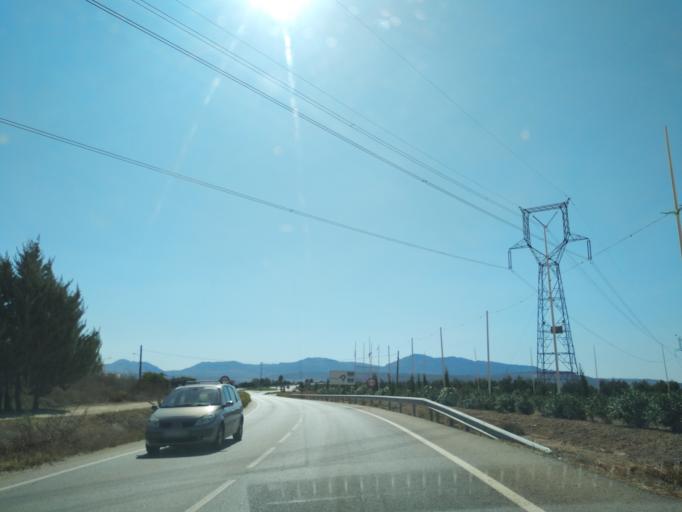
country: ES
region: Andalusia
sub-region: Provincia de Malaga
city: Mollina
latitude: 37.1000
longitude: -4.6347
